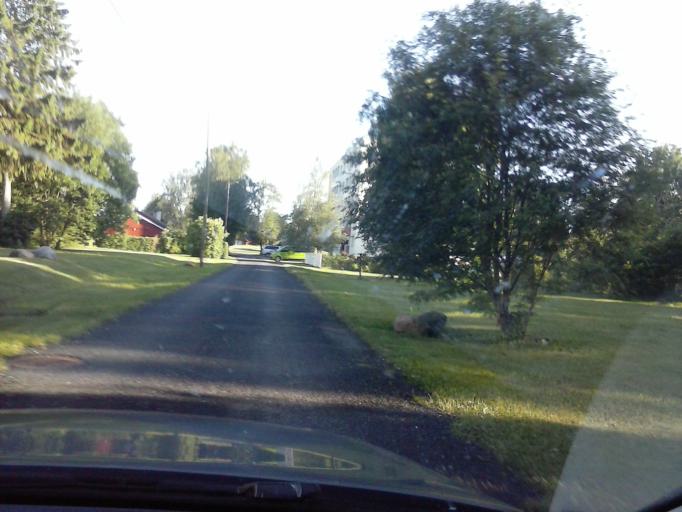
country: EE
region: Raplamaa
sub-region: Rapla vald
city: Rapla
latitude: 58.9989
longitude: 24.7853
